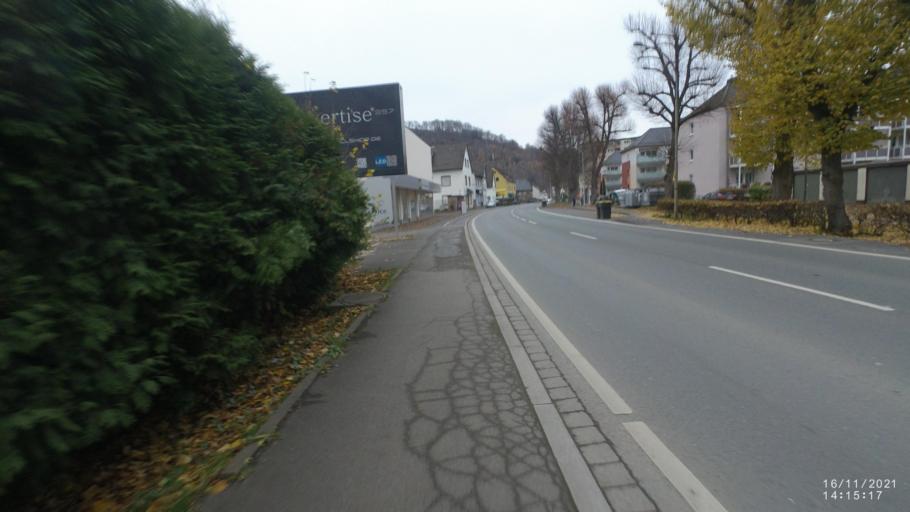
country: DE
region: North Rhine-Westphalia
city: Werdohl
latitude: 51.2521
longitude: 7.7476
